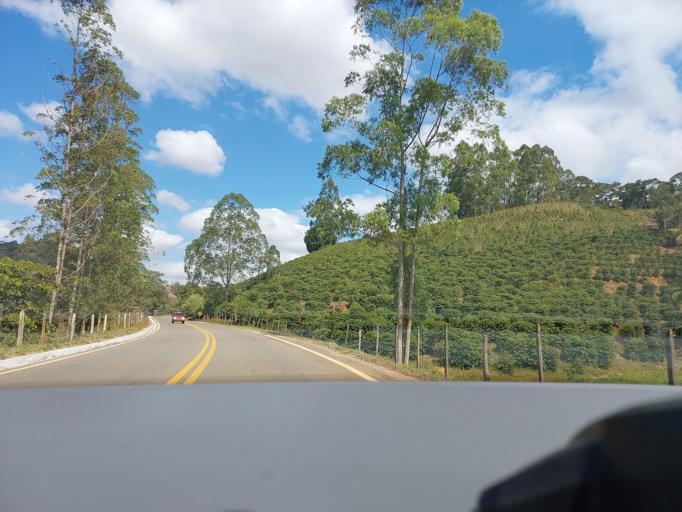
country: BR
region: Minas Gerais
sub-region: Mirai
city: Mirai
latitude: -21.0007
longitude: -42.5503
